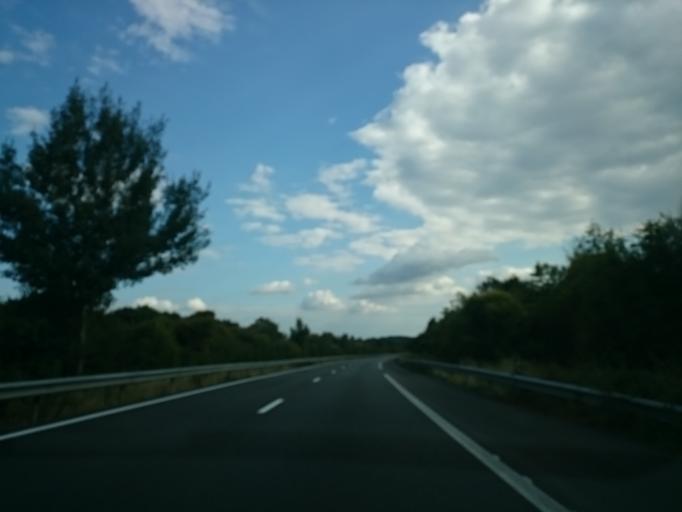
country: FR
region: Pays de la Loire
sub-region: Departement de la Loire-Atlantique
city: Jans
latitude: 47.6058
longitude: -1.6284
